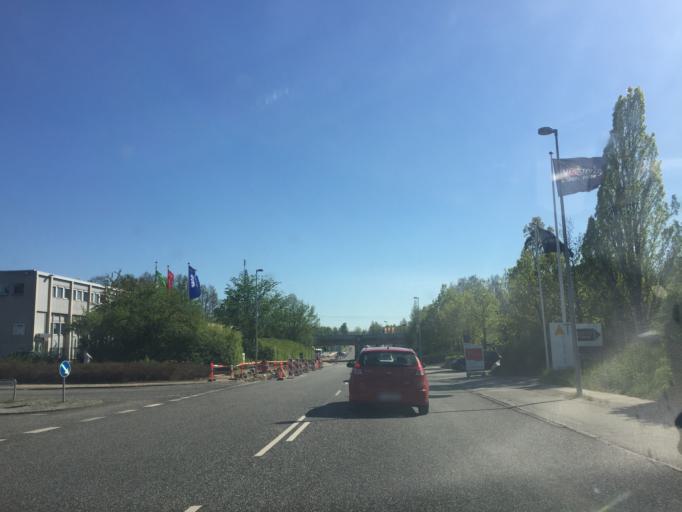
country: DK
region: Capital Region
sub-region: Ballerup Kommune
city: Ballerup
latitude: 55.7262
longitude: 12.3861
